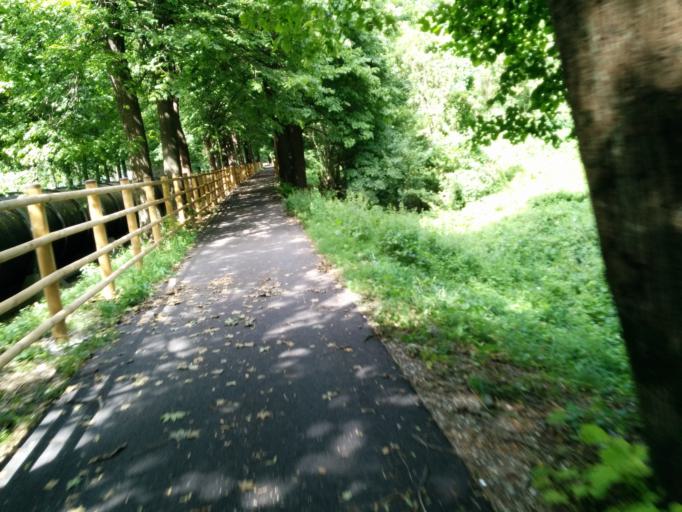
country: IT
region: Friuli Venezia Giulia
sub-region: Provincia di Udine
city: Lauco
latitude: 46.4076
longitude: 12.9472
